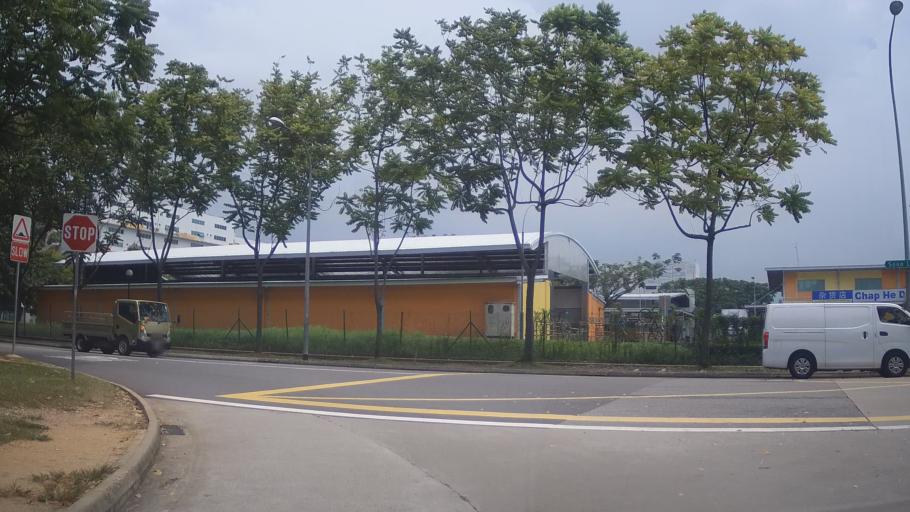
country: MY
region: Johor
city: Johor Bahru
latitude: 1.3323
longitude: 103.6982
